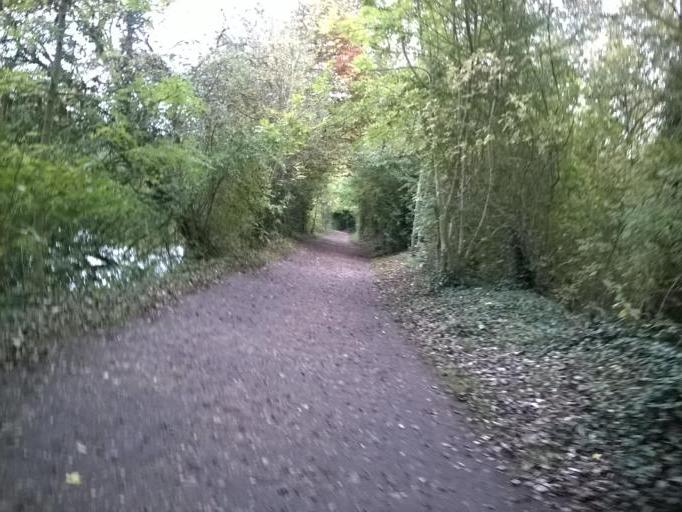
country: GB
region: England
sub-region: Wokingham
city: Sonning
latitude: 51.4669
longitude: -0.9259
